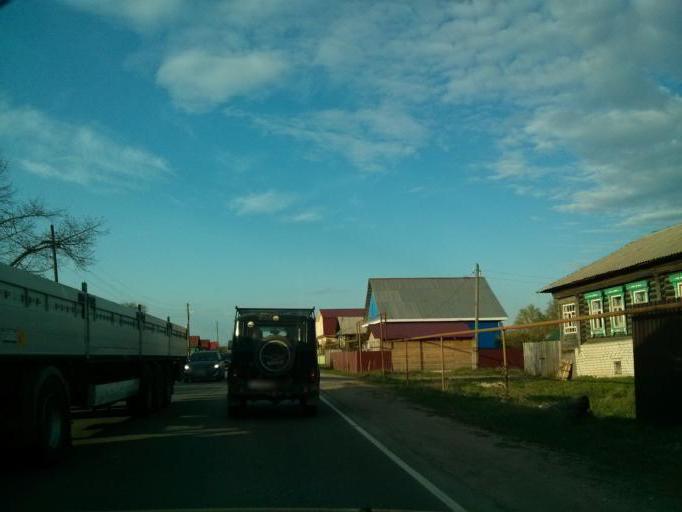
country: RU
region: Nizjnij Novgorod
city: Navashino
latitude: 55.6282
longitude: 42.2337
